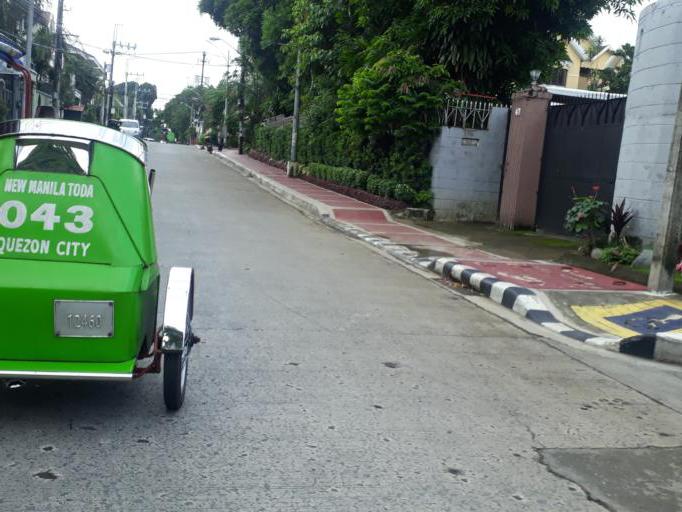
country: PH
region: Metro Manila
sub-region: San Juan
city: San Juan
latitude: 14.6192
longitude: 121.0255
